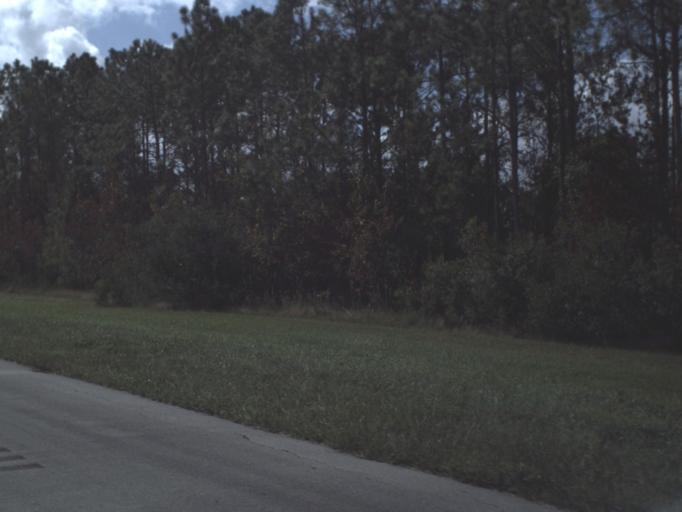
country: US
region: Florida
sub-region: Osceola County
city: Saint Cloud
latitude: 27.9171
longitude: -81.0561
